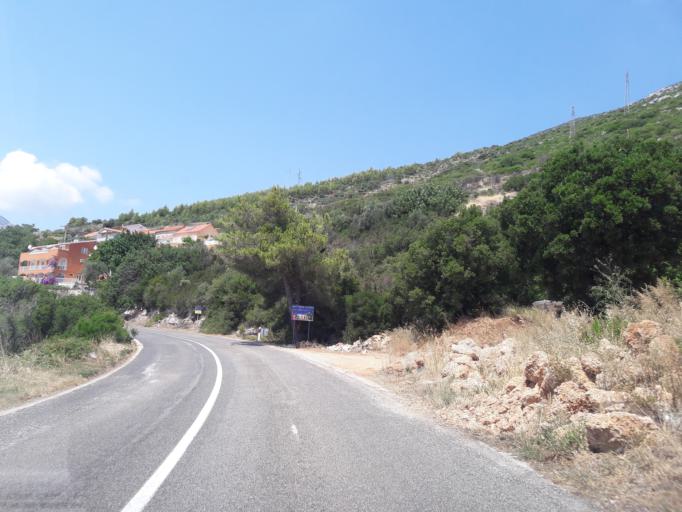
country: HR
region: Dubrovacko-Neretvanska
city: Orebic
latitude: 42.9784
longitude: 17.2276
